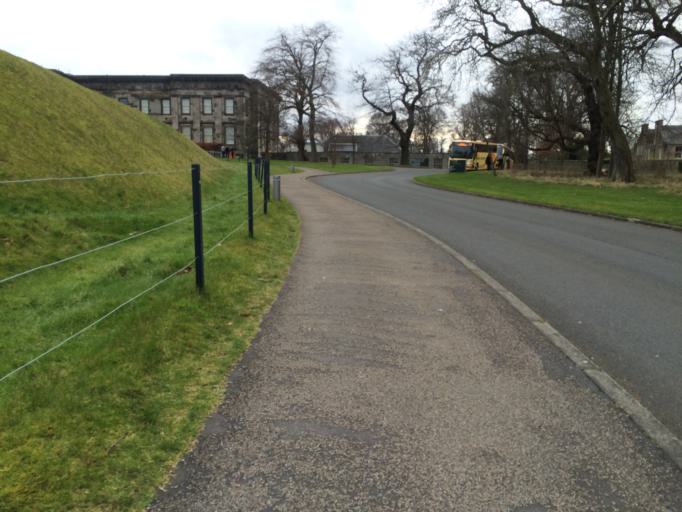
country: GB
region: Scotland
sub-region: Edinburgh
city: Edinburgh
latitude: 55.9518
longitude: -3.2270
